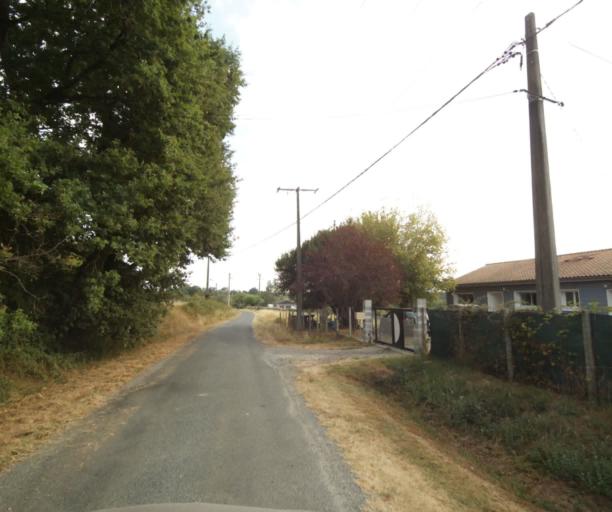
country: FR
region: Aquitaine
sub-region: Departement de la Gironde
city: Creon
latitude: 44.7639
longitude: -0.3578
